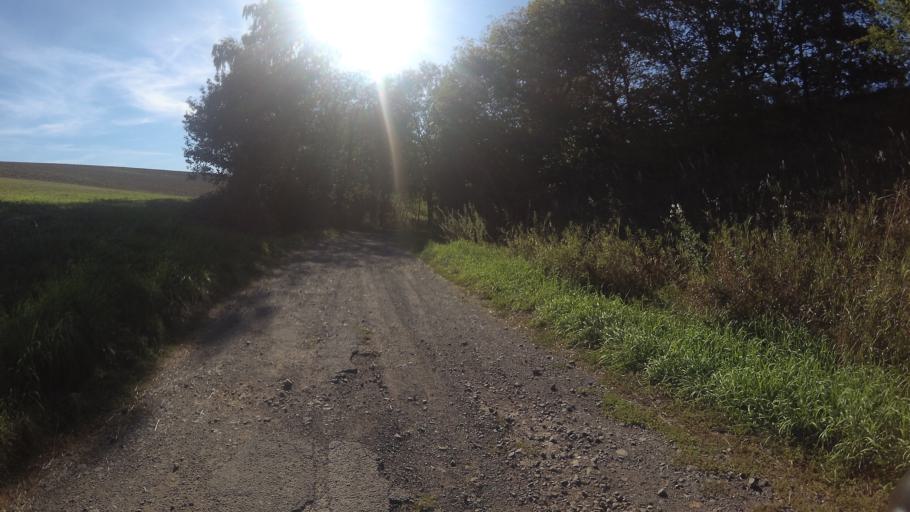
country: DE
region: Saarland
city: Tholey
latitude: 49.4756
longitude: 6.9796
